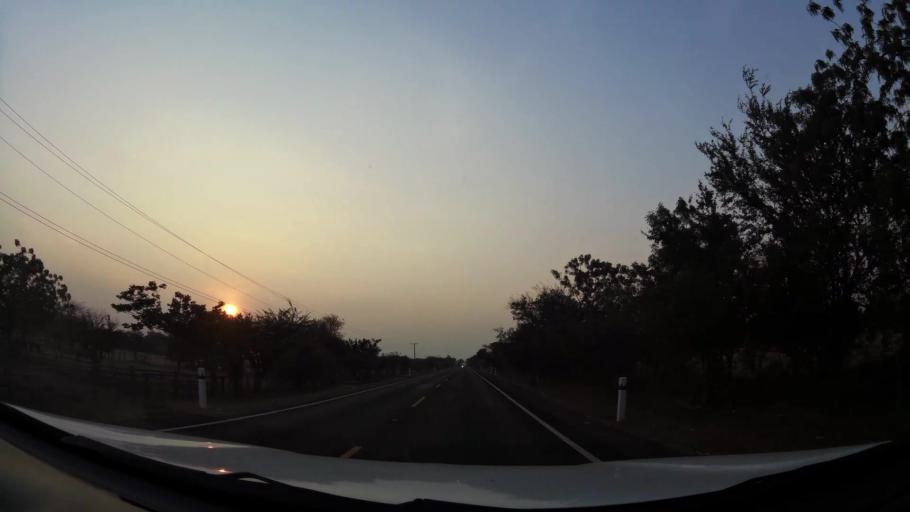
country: NI
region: Leon
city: La Paz Centro
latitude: 12.3172
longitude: -86.7909
